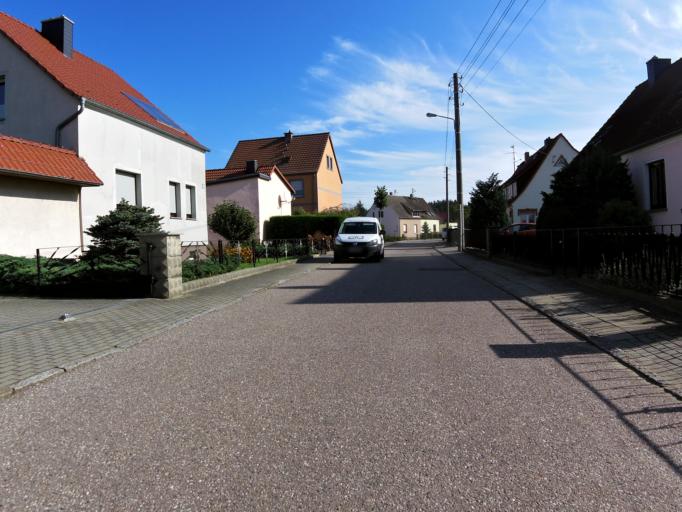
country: DE
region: Saxony-Anhalt
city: Coswig
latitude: 51.8737
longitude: 12.4744
